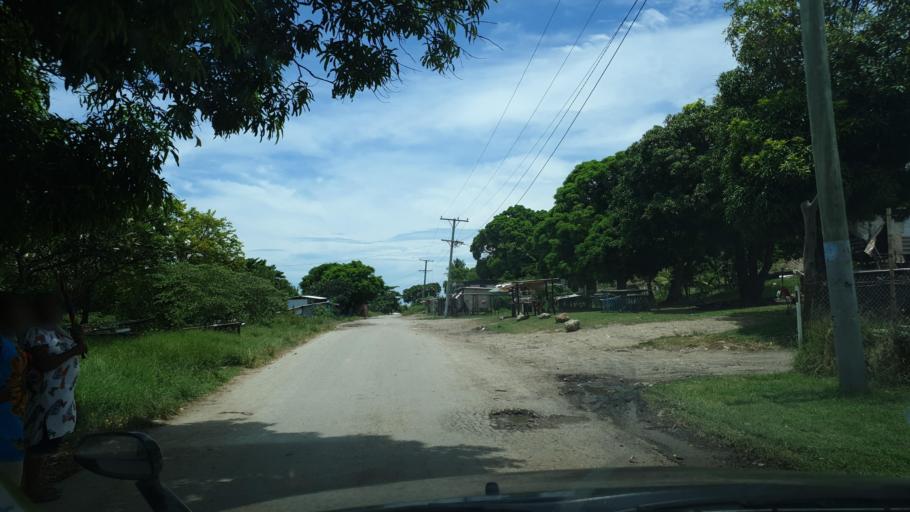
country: PG
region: National Capital
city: Port Moresby
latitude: -9.4224
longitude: 147.0480
